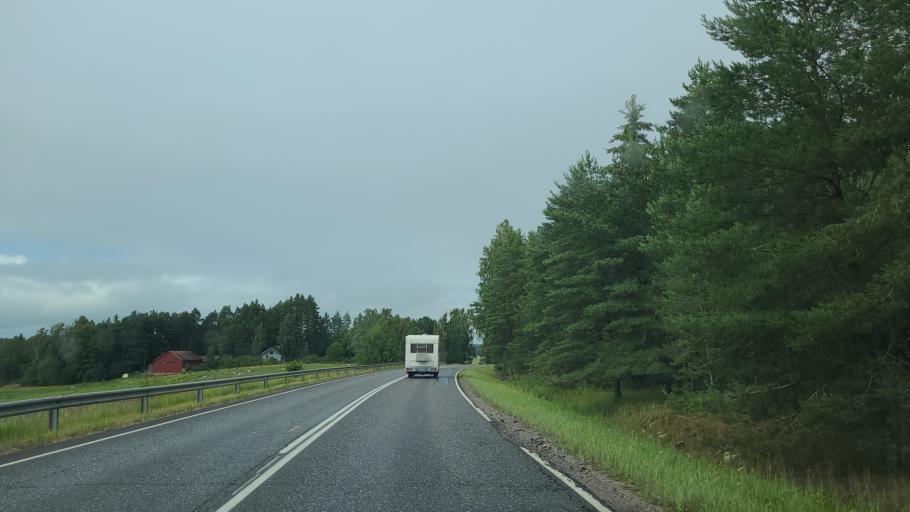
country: FI
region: Varsinais-Suomi
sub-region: Turku
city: Sauvo
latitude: 60.3095
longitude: 22.6875
